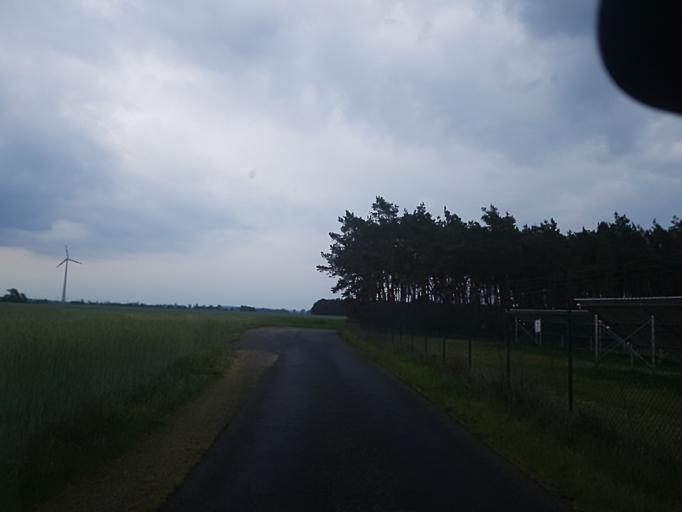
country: DE
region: Saxony-Anhalt
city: Elster
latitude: 51.8179
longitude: 12.8647
